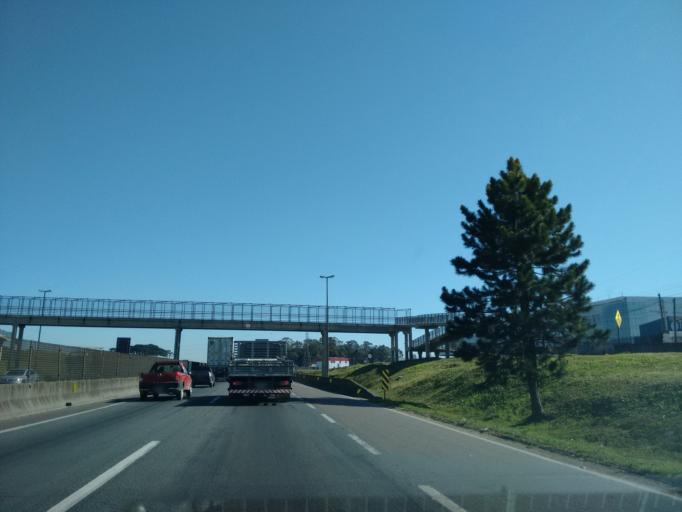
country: BR
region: Parana
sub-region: Sao Jose Dos Pinhais
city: Sao Jose dos Pinhais
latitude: -25.5477
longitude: -49.2877
